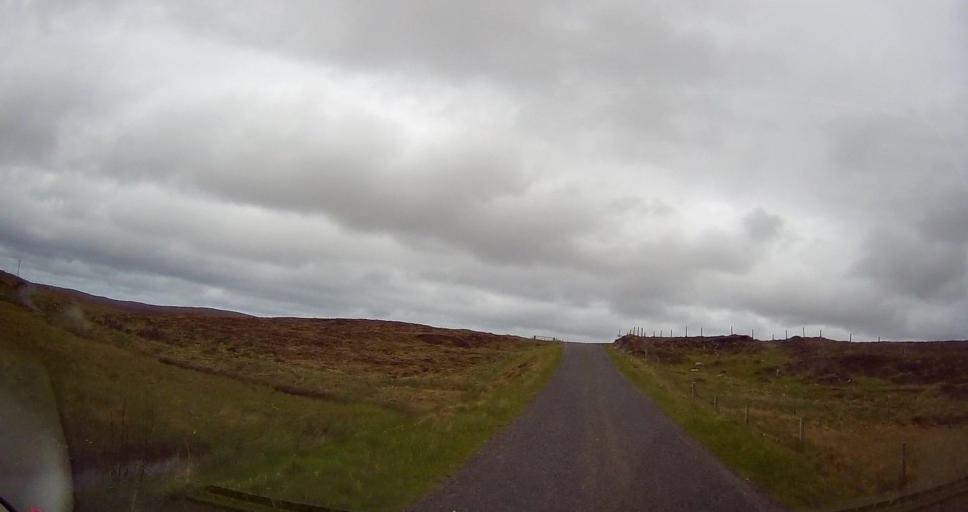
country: GB
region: Scotland
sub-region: Shetland Islands
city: Shetland
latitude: 60.7953
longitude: -0.8568
